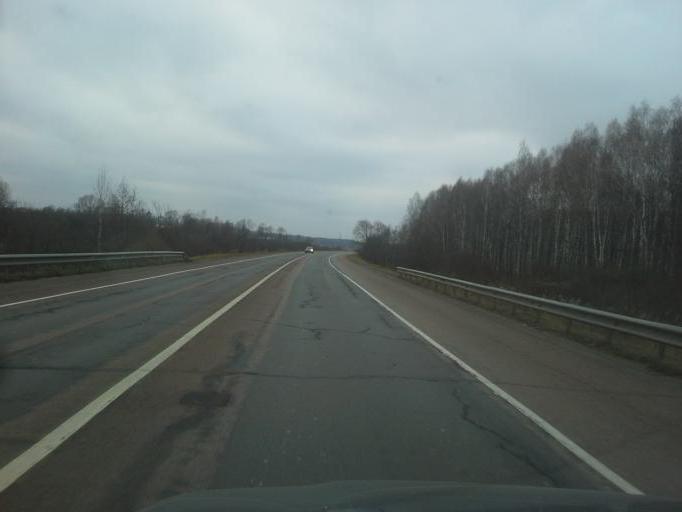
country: RU
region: Moskovskaya
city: Solnechnogorsk
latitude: 56.1456
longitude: 36.9407
